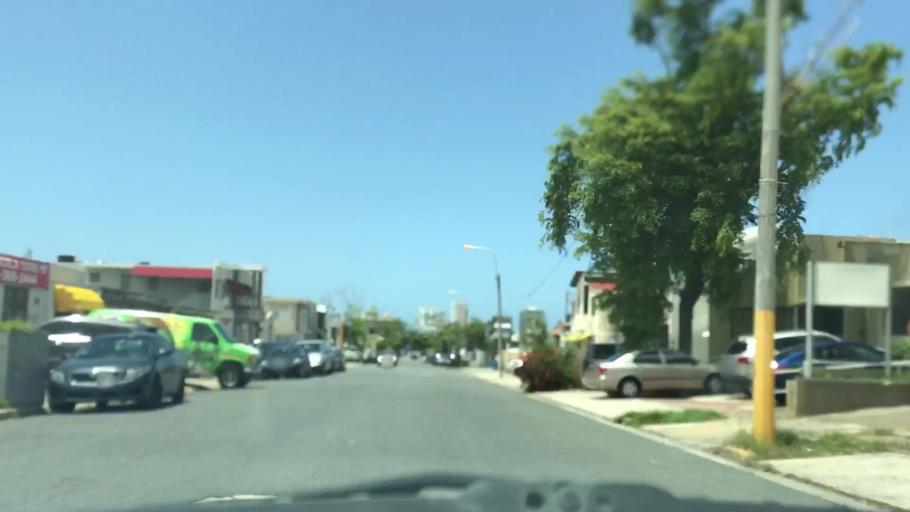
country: PR
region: Catano
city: Catano
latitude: 18.4150
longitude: -66.0617
